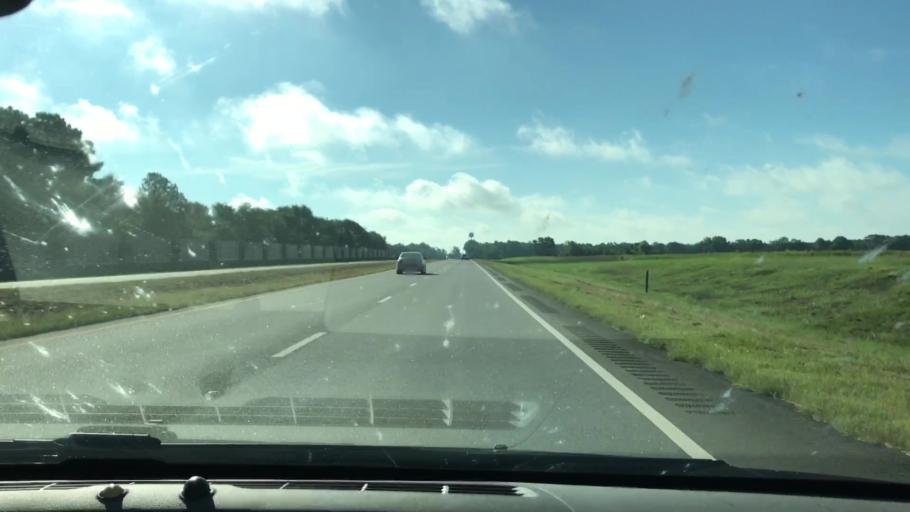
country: US
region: Georgia
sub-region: Terrell County
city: Dawson
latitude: 31.7281
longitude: -84.3611
